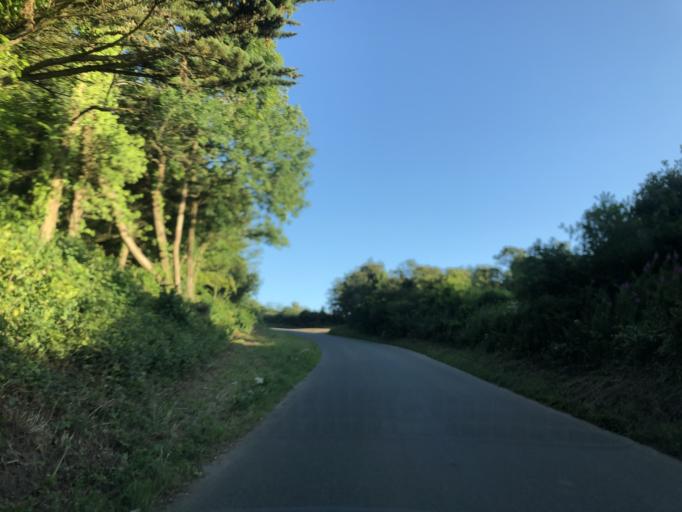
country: GB
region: England
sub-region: Isle of Wight
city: Shalfleet
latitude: 50.6597
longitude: -1.4064
